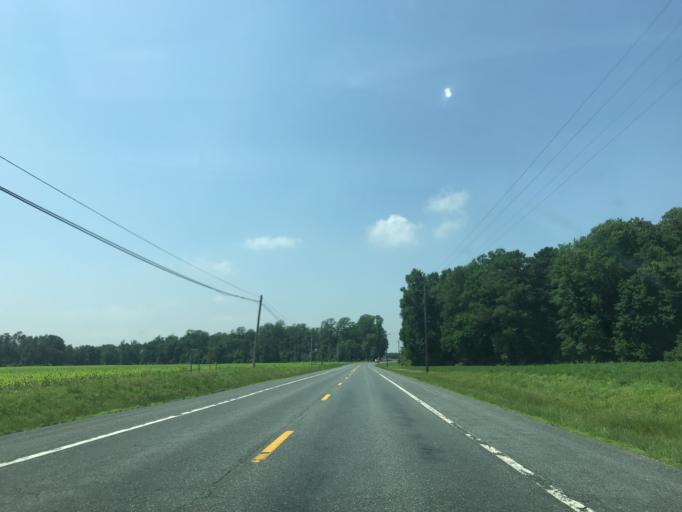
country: US
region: Maryland
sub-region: Caroline County
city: Federalsburg
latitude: 38.6612
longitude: -75.7333
